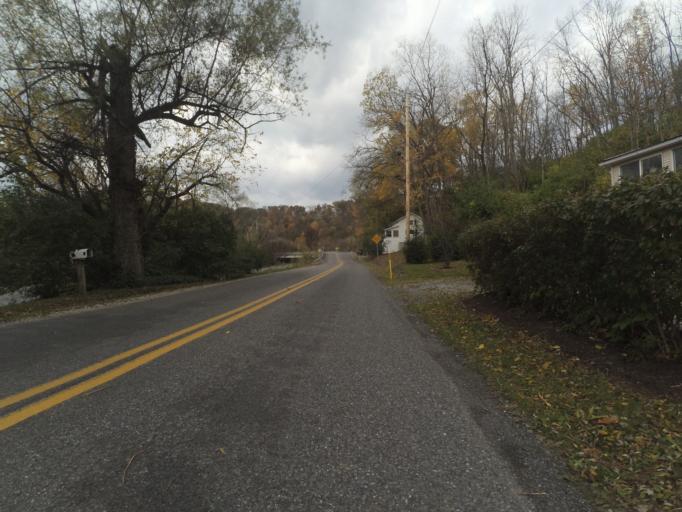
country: US
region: Pennsylvania
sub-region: Centre County
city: Bellefonte
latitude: 40.8893
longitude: -77.7928
